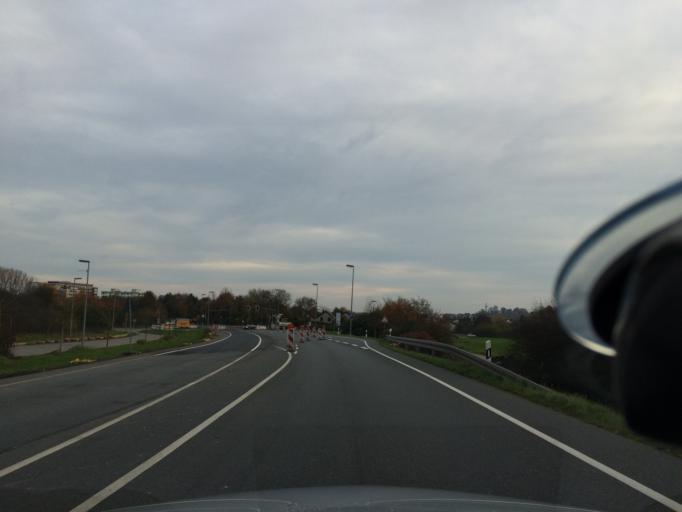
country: DE
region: Hesse
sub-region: Regierungsbezirk Darmstadt
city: Dietzenbach
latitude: 50.0220
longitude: 8.7705
